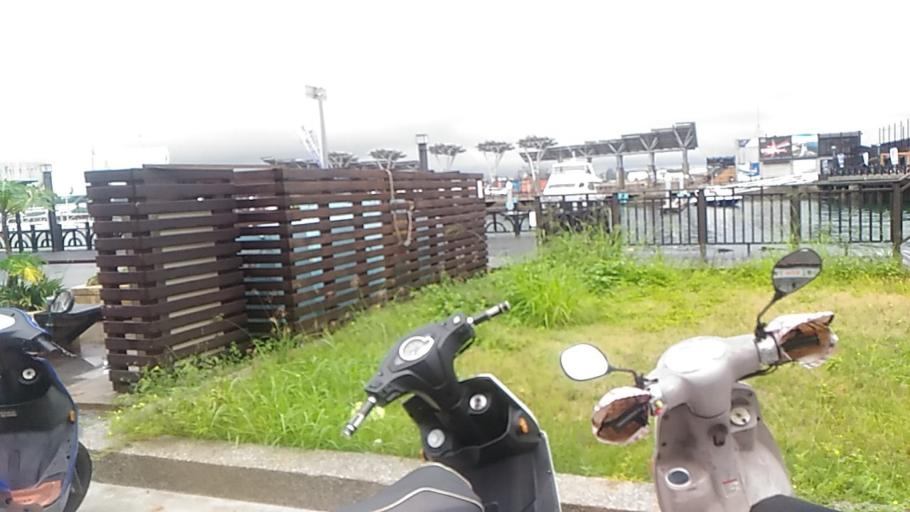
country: TW
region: Taiwan
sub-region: Penghu
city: Ma-kung
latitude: 23.5633
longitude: 119.5673
